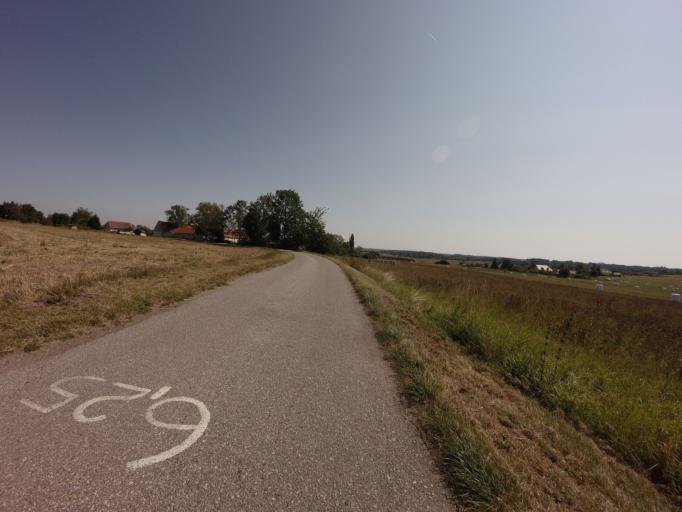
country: CZ
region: Jihocesky
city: Kamenny Ujezd
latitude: 48.8818
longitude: 14.3846
